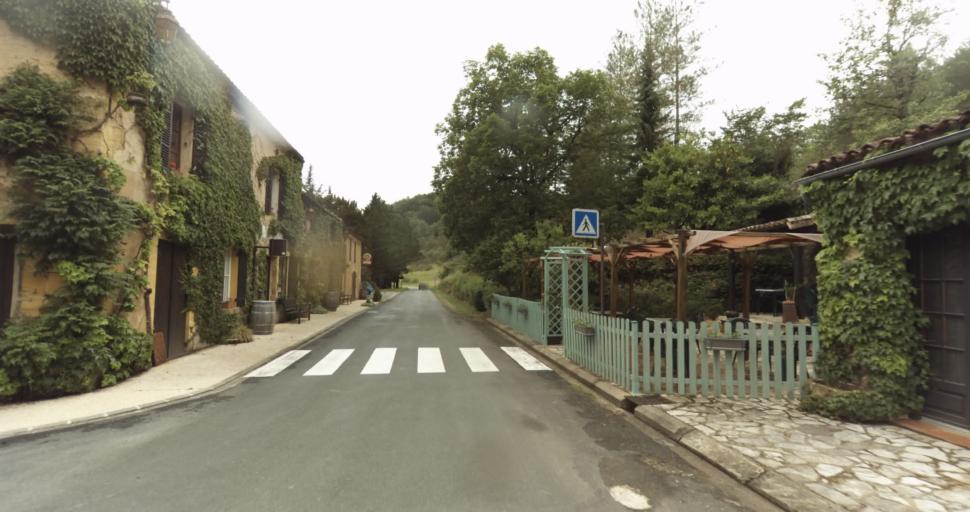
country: FR
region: Aquitaine
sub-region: Departement de la Dordogne
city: Beaumont-du-Perigord
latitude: 44.7535
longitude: 0.8691
